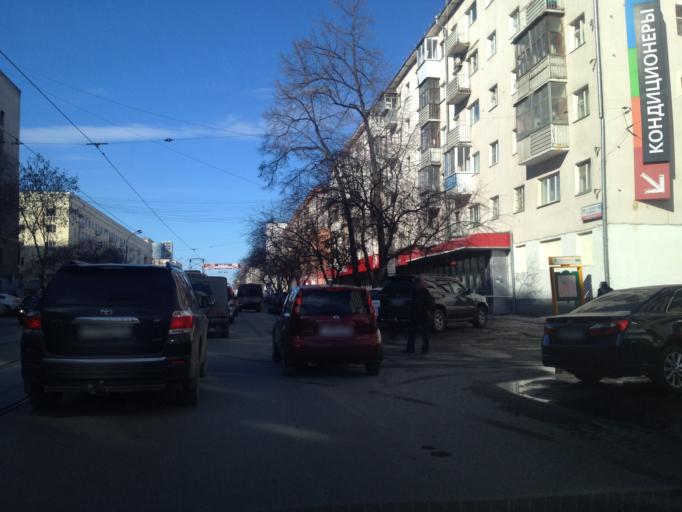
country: RU
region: Sverdlovsk
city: Yekaterinburg
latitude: 56.8372
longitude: 60.6216
